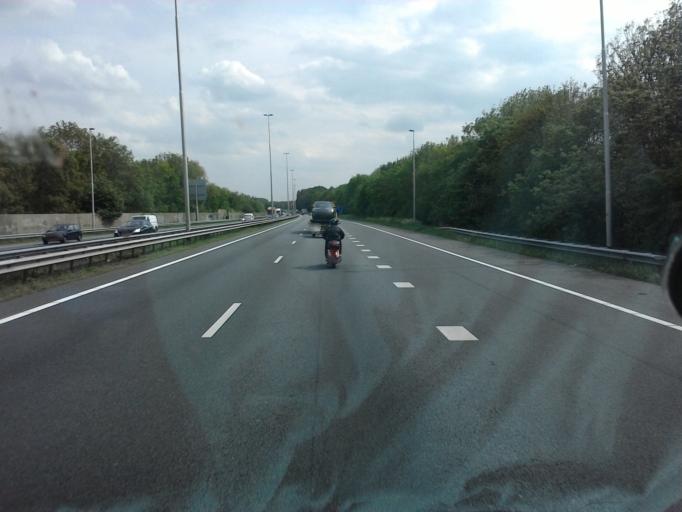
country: NL
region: Gelderland
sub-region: Gemeente Nijmegen
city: Lindenholt
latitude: 51.8187
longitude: 5.7764
